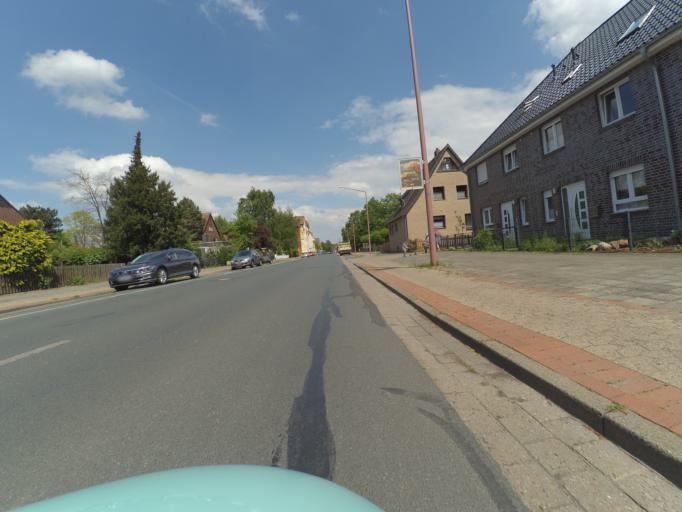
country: DE
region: Lower Saxony
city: Lehrte
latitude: 52.3661
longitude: 9.9651
